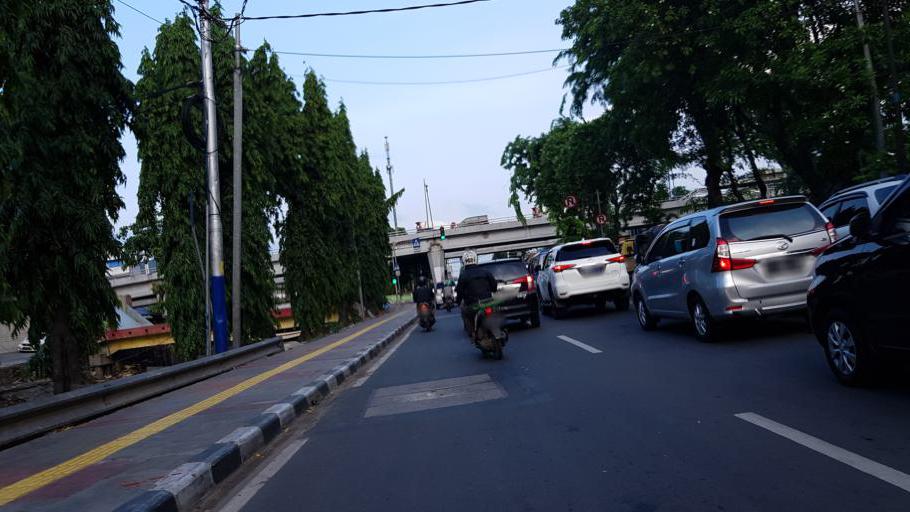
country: ID
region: Jakarta Raya
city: Jakarta
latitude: -6.1429
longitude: 106.7926
